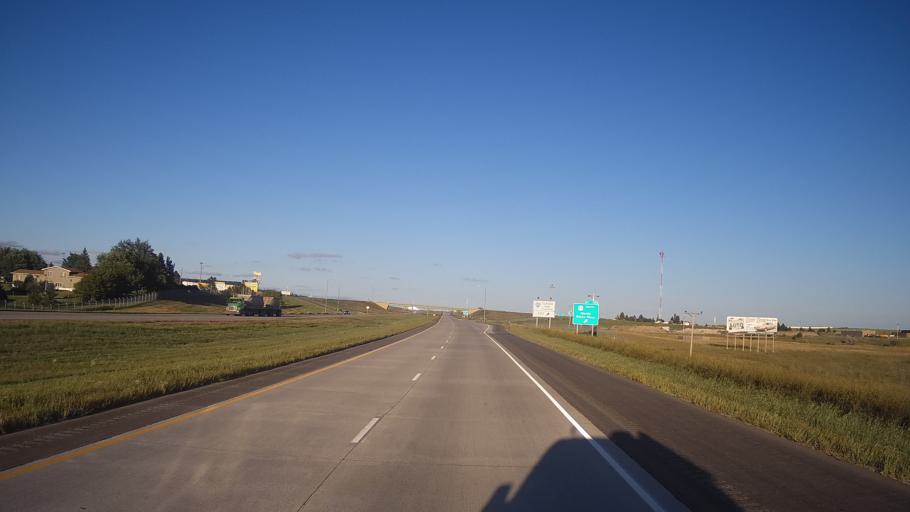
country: US
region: South Dakota
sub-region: Jones County
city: Murdo
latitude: 43.8831
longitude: -100.7143
